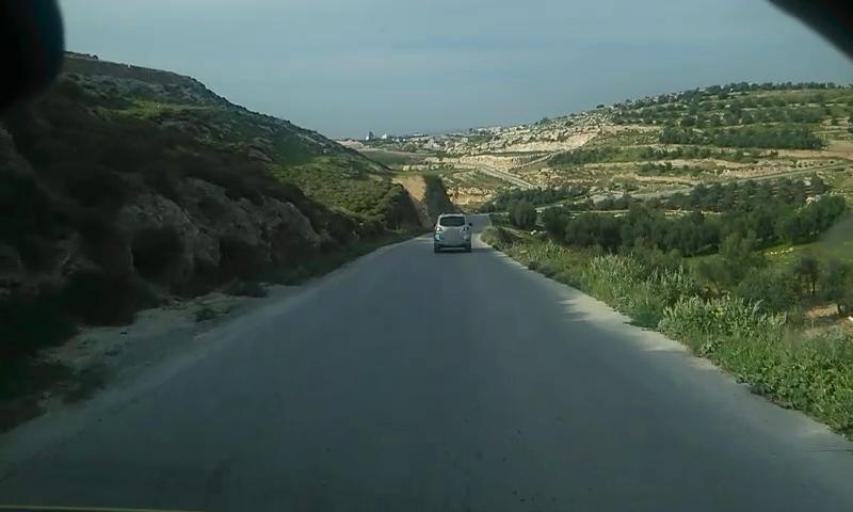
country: PS
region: West Bank
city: Nuba
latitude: 31.6123
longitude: 35.0184
